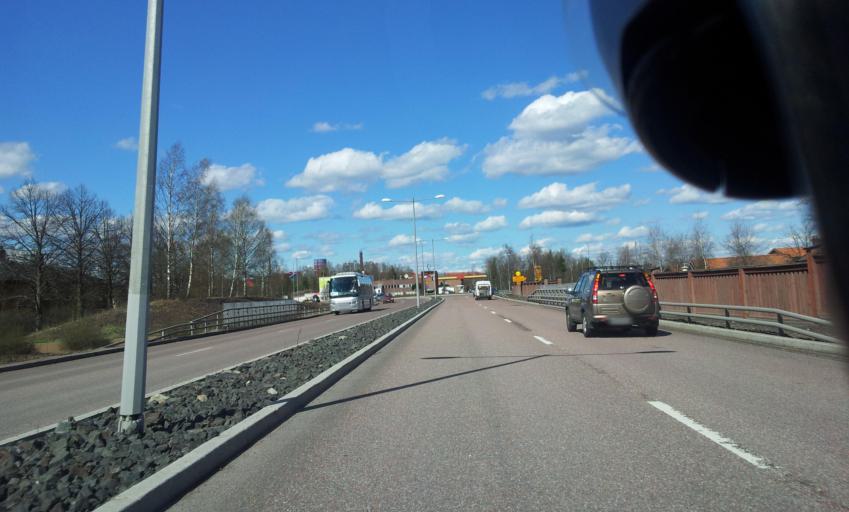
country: SE
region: Dalarna
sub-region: Faluns Kommun
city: Falun
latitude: 60.6002
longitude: 15.6220
